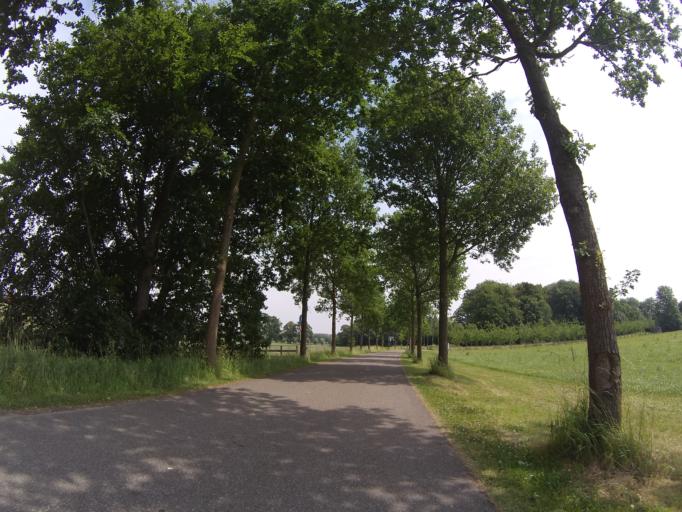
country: NL
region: Utrecht
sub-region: Gemeente Bunnik
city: Bunnik
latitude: 52.0767
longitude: 5.1836
